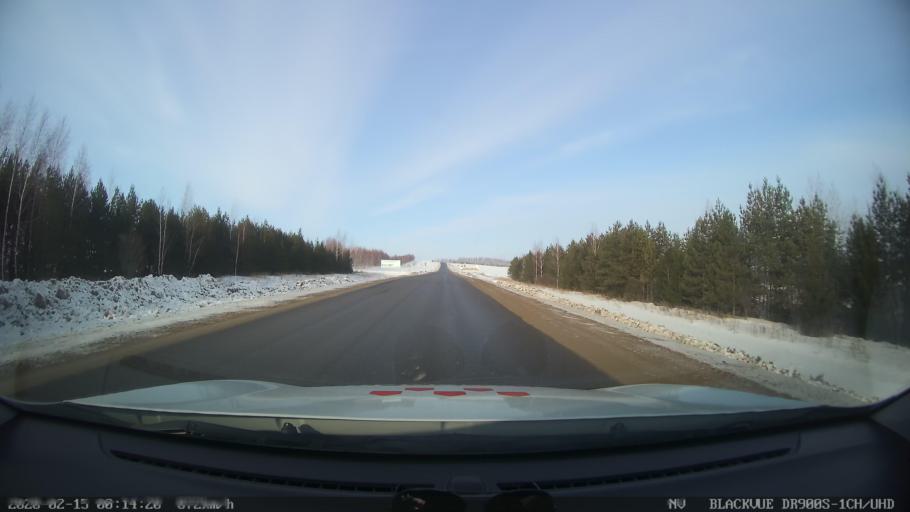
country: RU
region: Tatarstan
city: Stolbishchi
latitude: 55.4848
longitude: 49.0044
